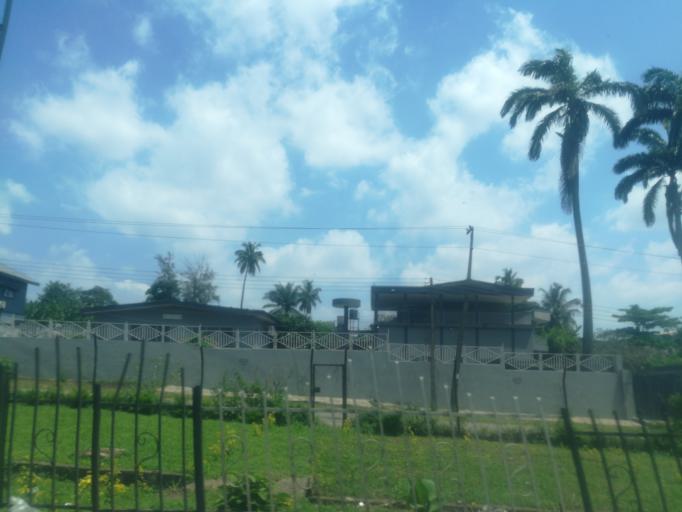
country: NG
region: Oyo
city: Ibadan
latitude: 7.3715
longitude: 3.8597
